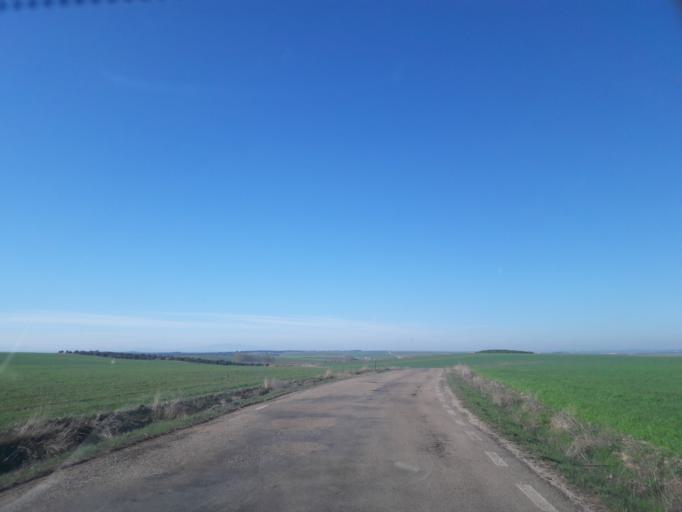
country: ES
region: Castille and Leon
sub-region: Provincia de Salamanca
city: Tordillos
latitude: 40.8695
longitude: -5.3332
